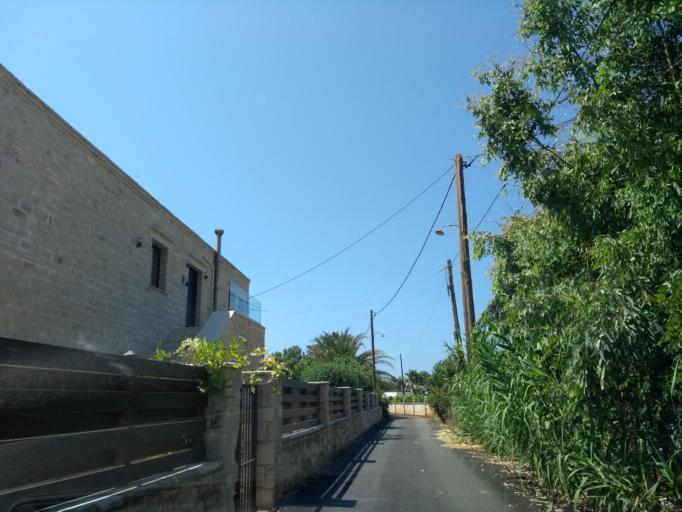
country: GR
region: Crete
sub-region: Nomos Rethymnis
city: Atsipopoulon
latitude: 35.3573
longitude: 24.3683
